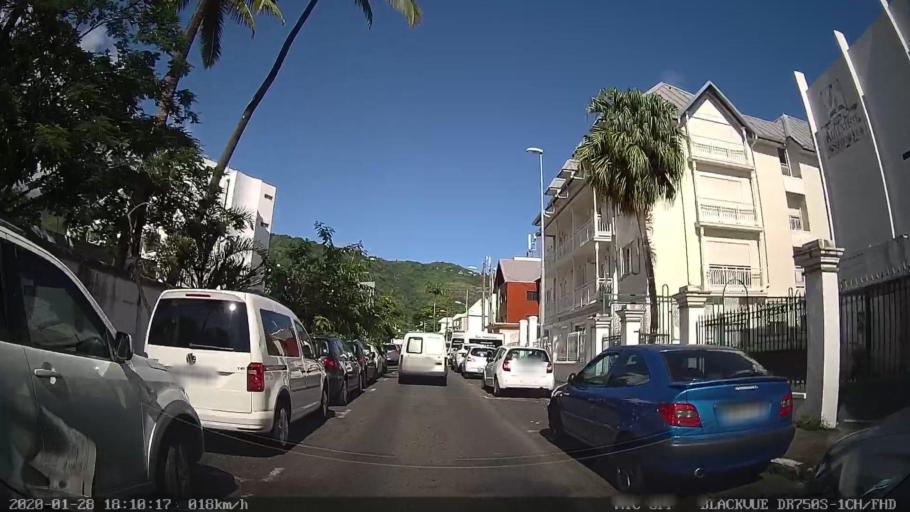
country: RE
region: Reunion
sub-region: Reunion
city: Saint-Denis
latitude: -20.8857
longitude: 55.4501
